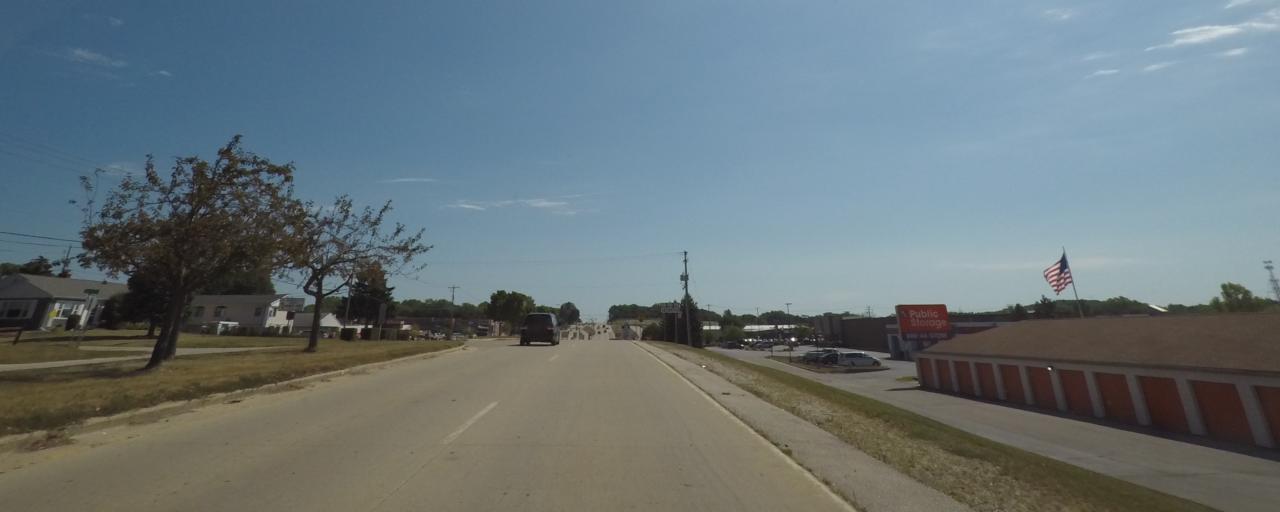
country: US
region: Wisconsin
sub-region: Waukesha County
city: Waukesha
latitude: 43.0138
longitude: -88.2038
